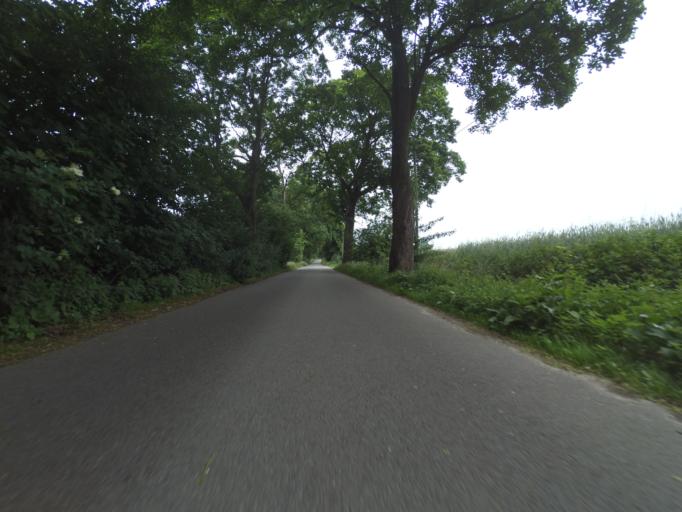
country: DE
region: Mecklenburg-Vorpommern
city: Dabel
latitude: 53.6641
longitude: 11.9395
